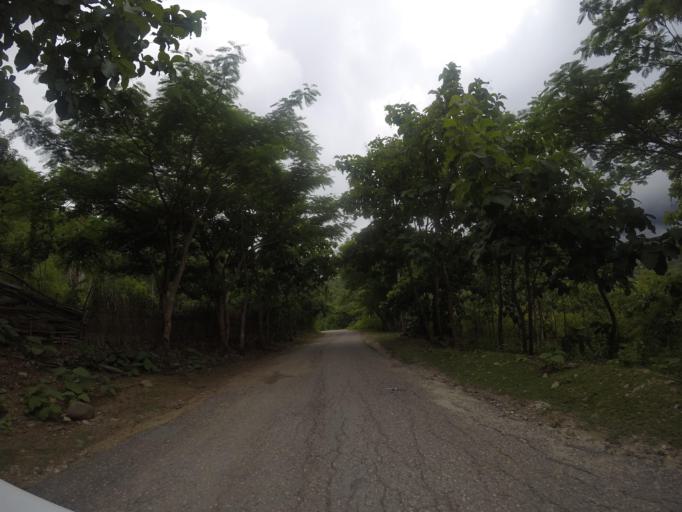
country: TL
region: Bobonaro
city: Maliana
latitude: -8.9638
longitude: 125.0303
